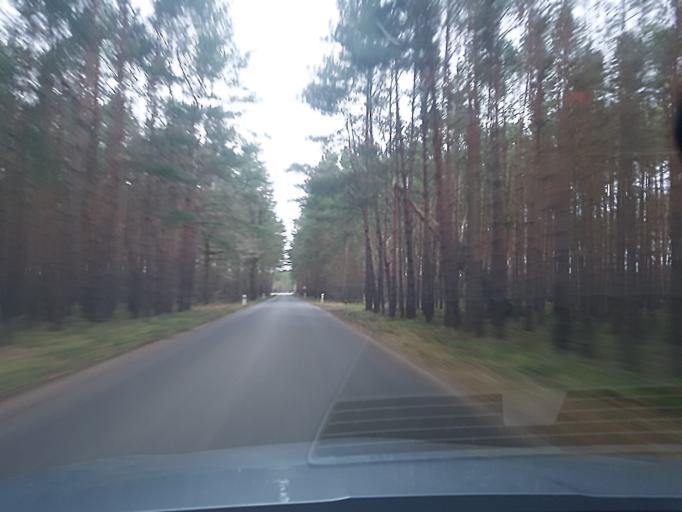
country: DE
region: Brandenburg
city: Schilda
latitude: 51.5678
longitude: 13.3337
